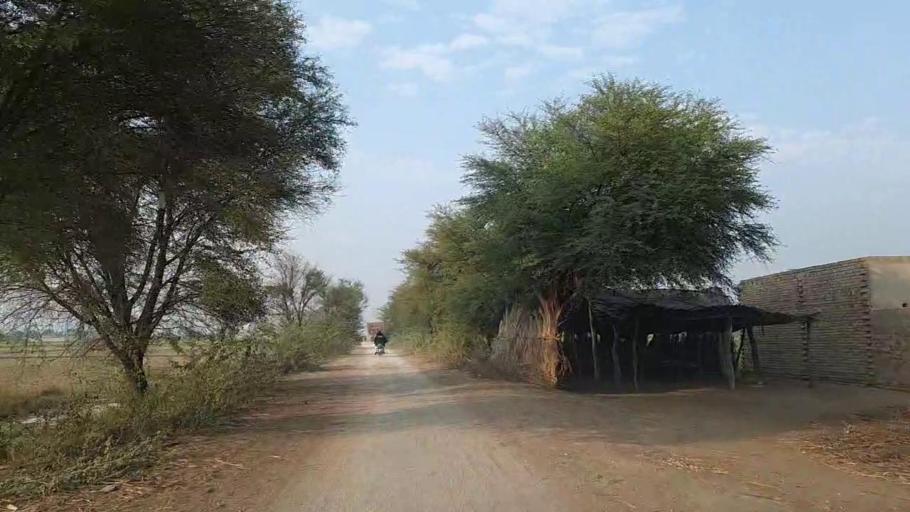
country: PK
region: Sindh
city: Jam Sahib
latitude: 26.3236
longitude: 68.5530
